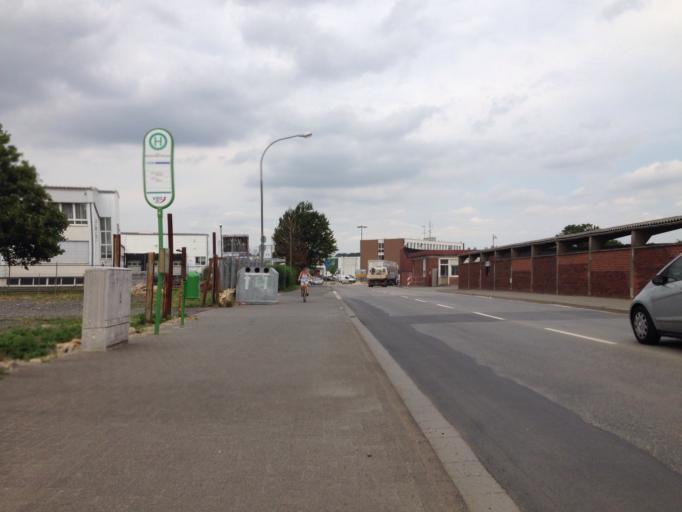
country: DE
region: Hesse
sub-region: Regierungsbezirk Giessen
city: Giessen
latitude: 50.5687
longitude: 8.6953
